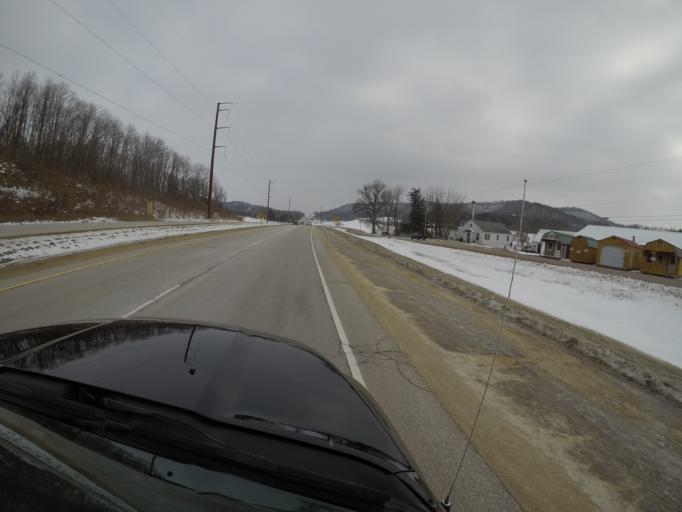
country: US
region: Wisconsin
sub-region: Trempealeau County
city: Galesville
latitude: 44.0769
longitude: -91.3490
